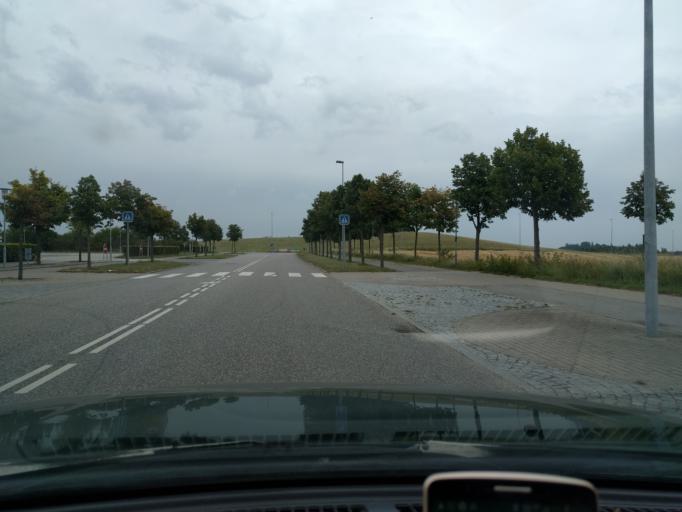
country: DK
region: Zealand
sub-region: Slagelse Kommune
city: Korsor
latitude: 55.3563
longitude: 11.1355
